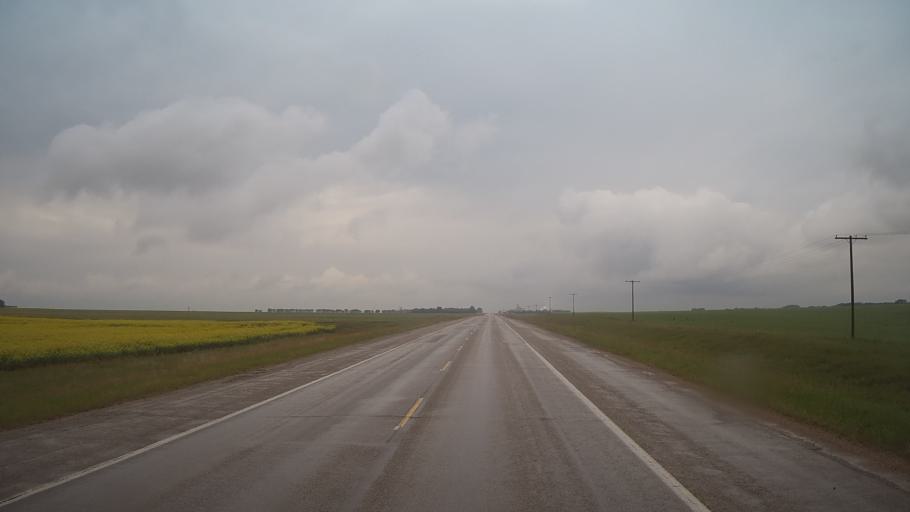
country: CA
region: Saskatchewan
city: Unity
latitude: 52.4350
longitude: -109.0593
